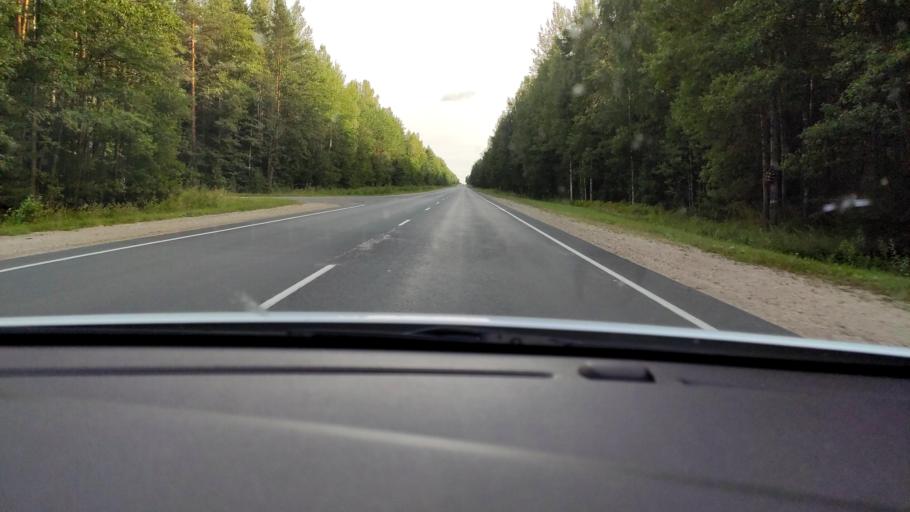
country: RU
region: Mariy-El
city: Suslonger
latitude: 56.2708
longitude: 48.2330
